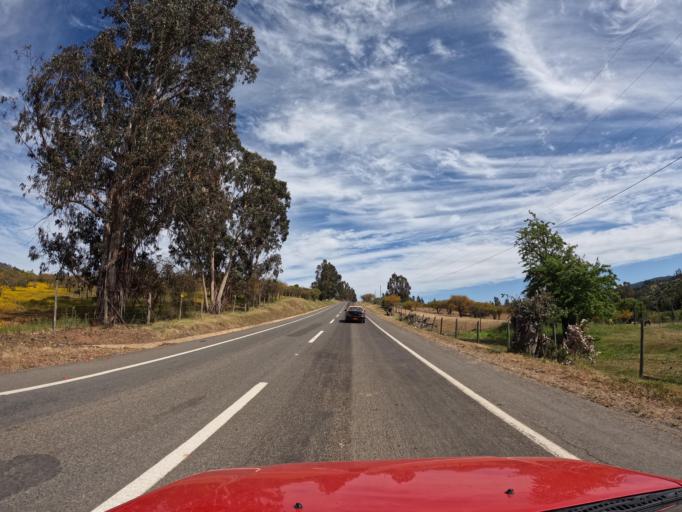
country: CL
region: Maule
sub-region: Provincia de Talca
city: Talca
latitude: -35.1196
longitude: -71.9584
